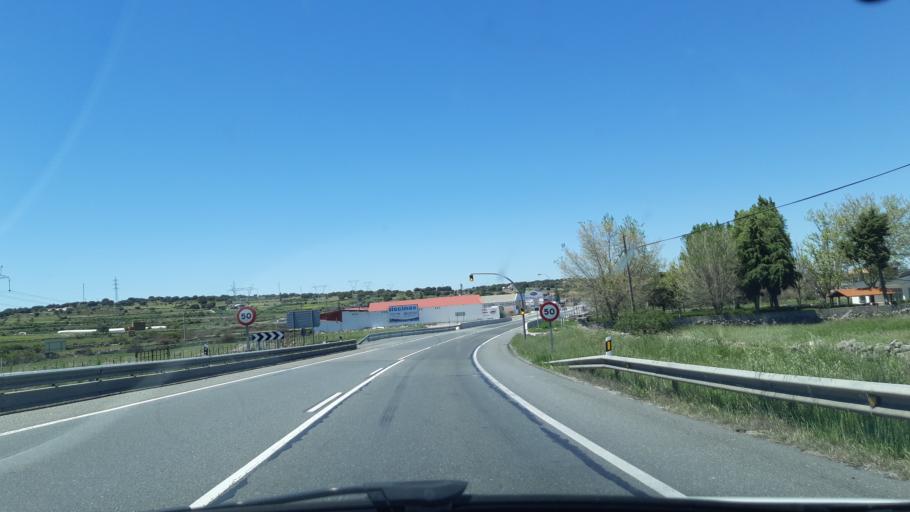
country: ES
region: Castille and Leon
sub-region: Provincia de Segovia
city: Zarzuela del Monte
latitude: 40.7559
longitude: -4.3273
